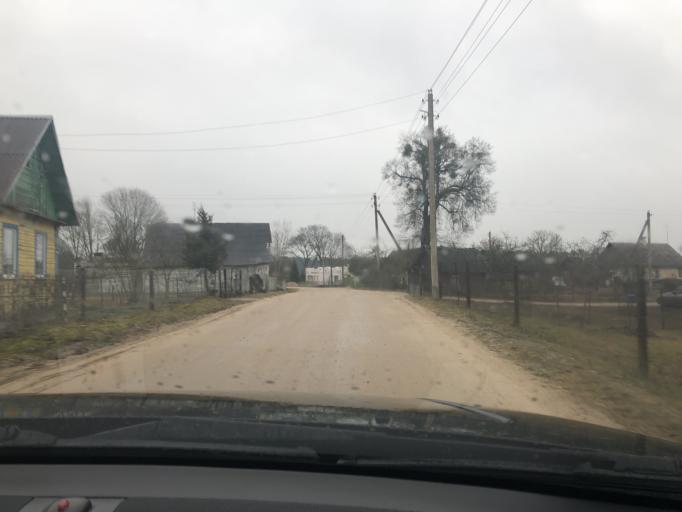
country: BY
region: Grodnenskaya
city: Skidal'
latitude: 53.8601
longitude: 24.2454
